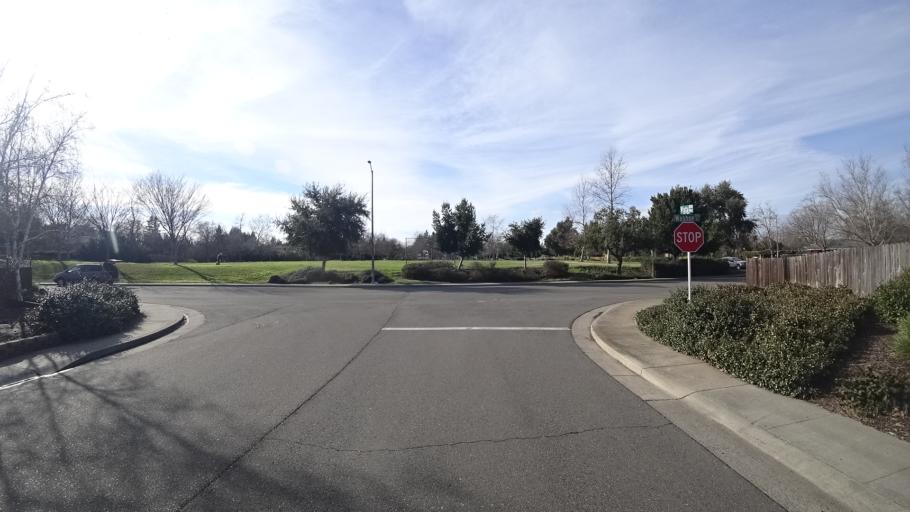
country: US
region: California
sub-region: Yolo County
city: Davis
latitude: 38.5470
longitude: -121.7041
